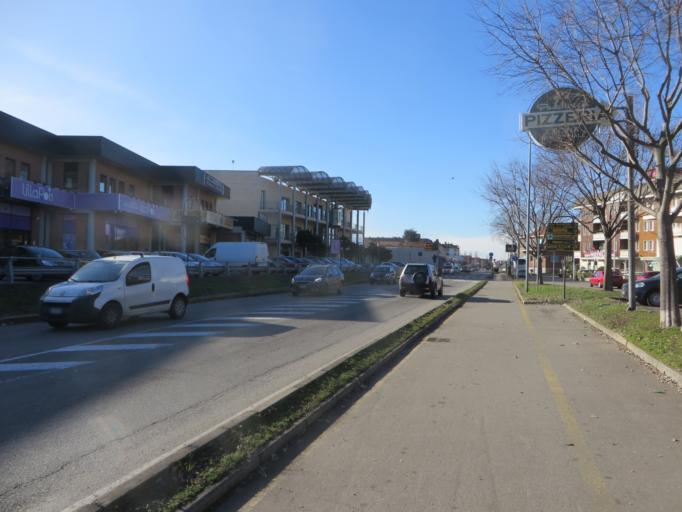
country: IT
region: Lombardy
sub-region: Citta metropolitana di Milano
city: Bareggio
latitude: 45.4855
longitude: 9.0003
